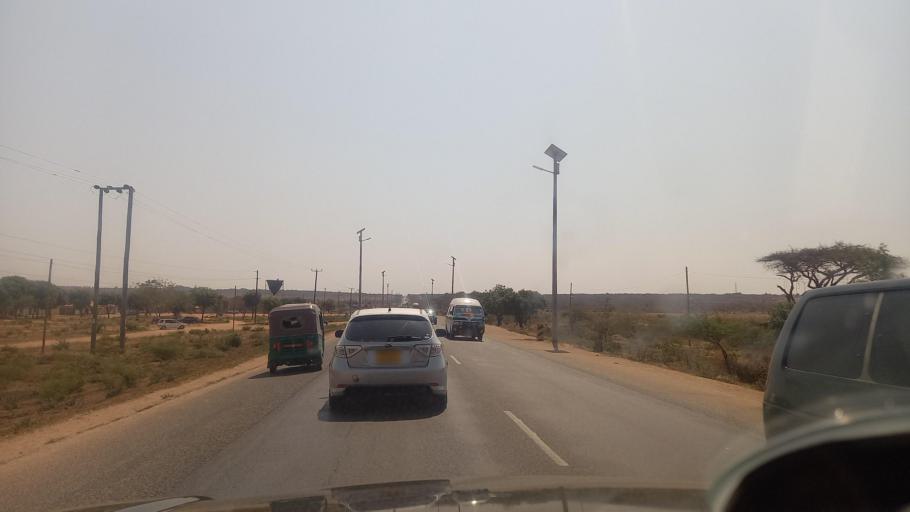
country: TZ
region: Dodoma
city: Kisasa
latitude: -6.1453
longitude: 35.8274
